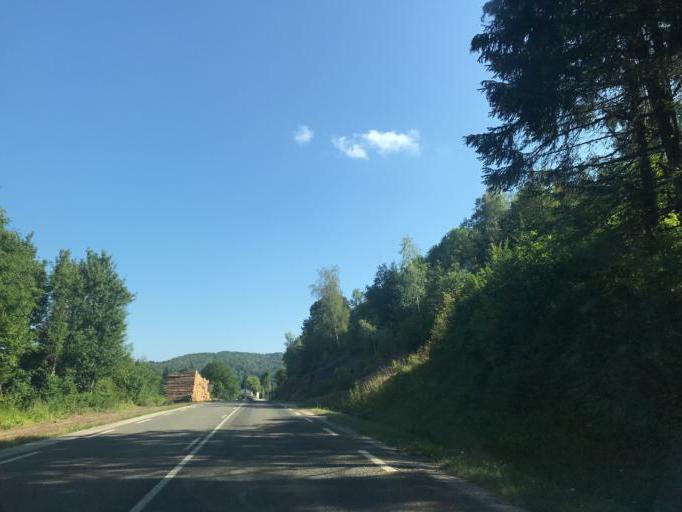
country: FR
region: Franche-Comte
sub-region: Departement du Jura
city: Moirans-en-Montagne
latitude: 46.4055
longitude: 5.7342
